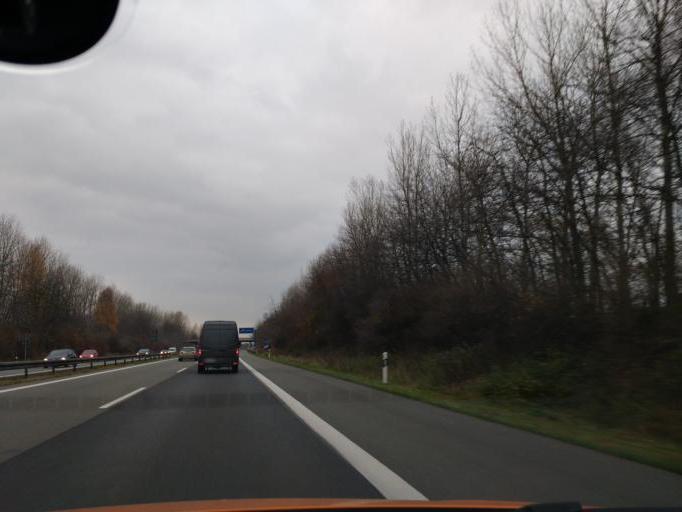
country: DE
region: Brandenburg
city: Fehrbellin
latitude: 52.8000
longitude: 12.7950
